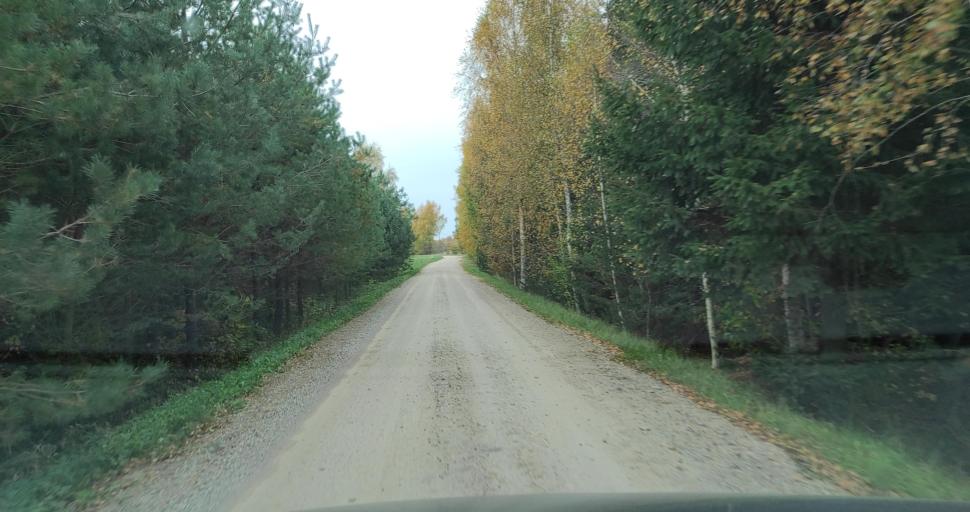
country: LV
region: Kuldigas Rajons
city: Kuldiga
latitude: 57.0269
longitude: 22.1985
